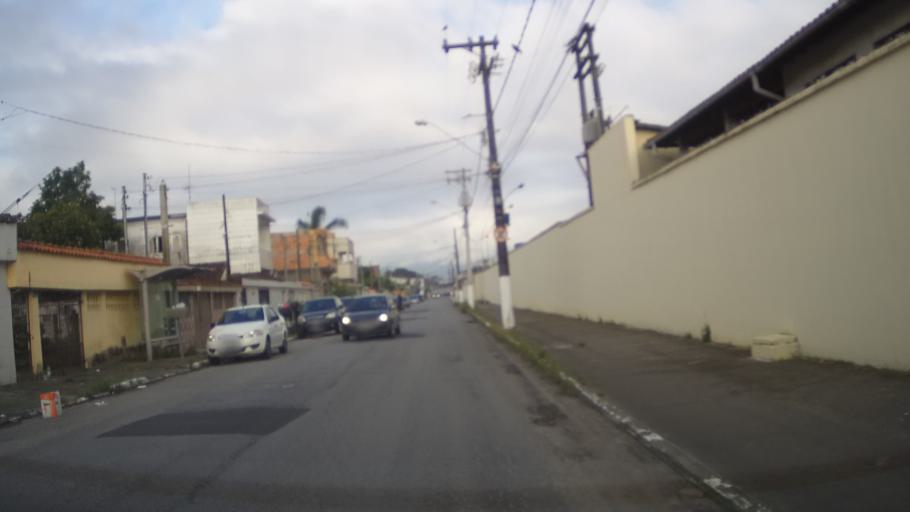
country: BR
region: Sao Paulo
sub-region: Praia Grande
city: Praia Grande
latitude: -24.0185
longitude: -46.4782
